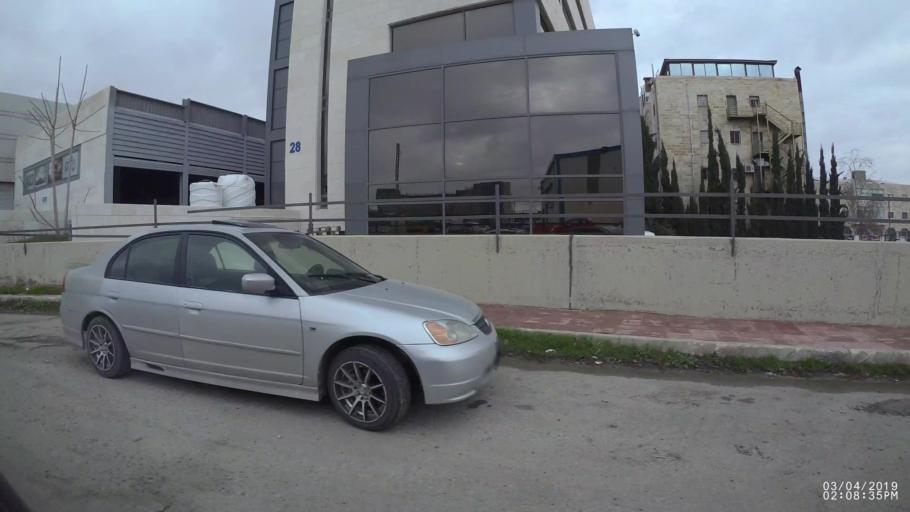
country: JO
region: Amman
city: Wadi as Sir
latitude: 31.9446
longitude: 35.8424
